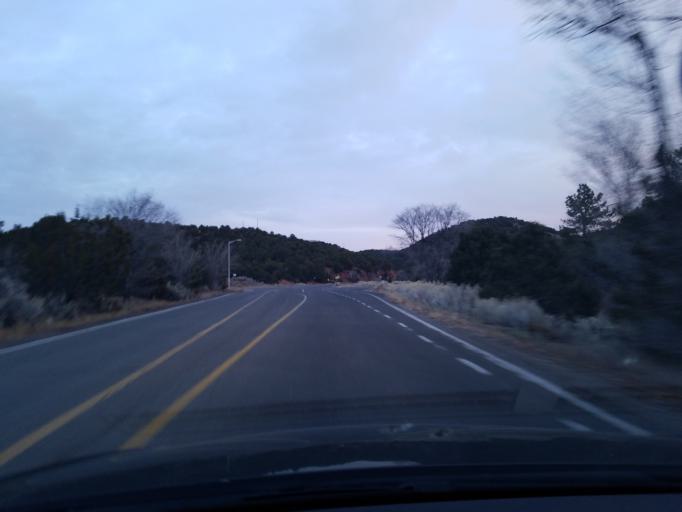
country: US
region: New Mexico
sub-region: Santa Fe County
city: Santa Fe
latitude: 35.7089
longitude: -105.8995
